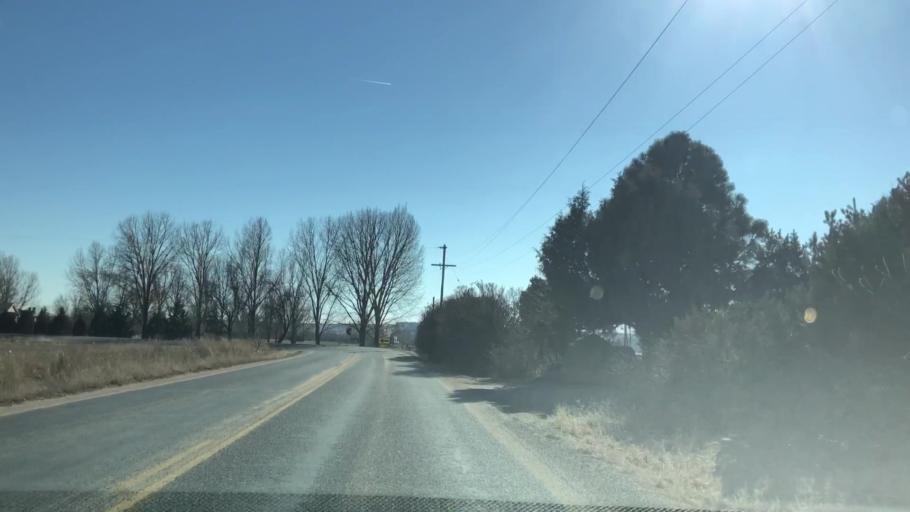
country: US
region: Colorado
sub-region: Weld County
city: Windsor
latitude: 40.4908
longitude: -104.9441
